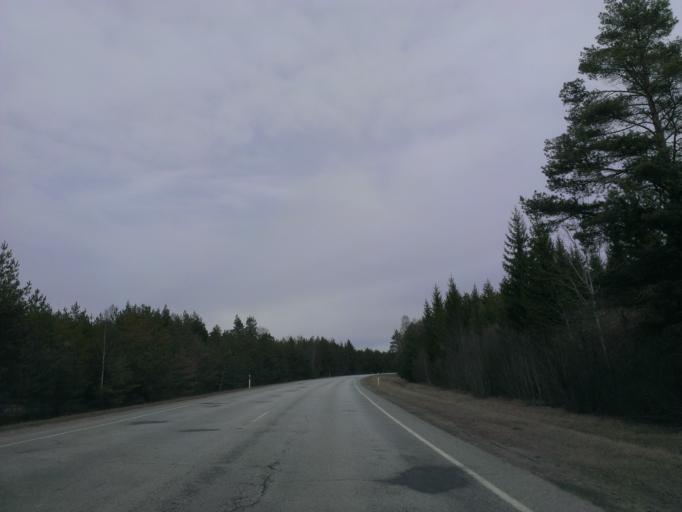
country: EE
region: Laeaene
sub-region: Lihula vald
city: Lihula
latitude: 58.6034
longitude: 23.5557
